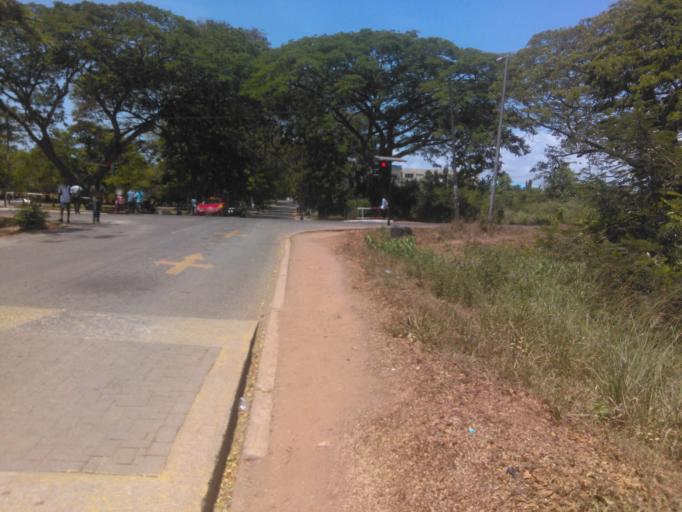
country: GH
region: Central
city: Cape Coast
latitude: 5.1175
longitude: -1.2863
